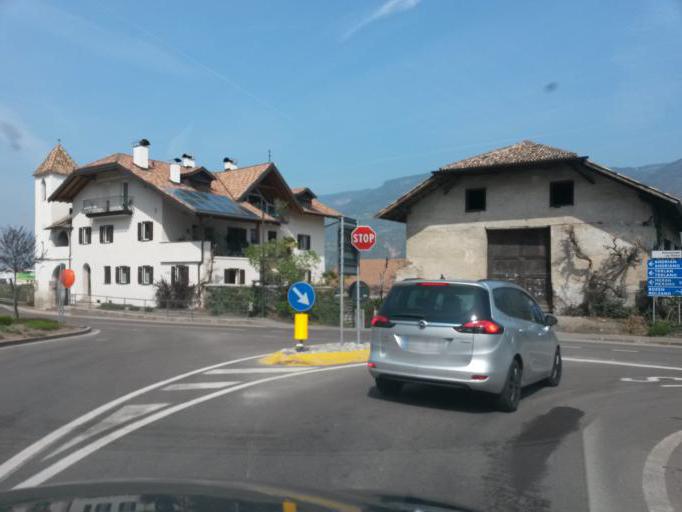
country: IT
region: Trentino-Alto Adige
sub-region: Bolzano
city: San Paolo
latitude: 46.4909
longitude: 11.2599
